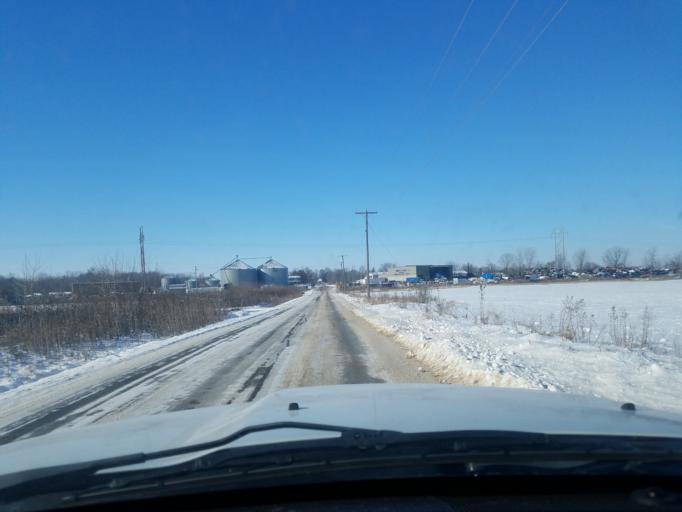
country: US
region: Indiana
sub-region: Noble County
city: Kendallville
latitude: 41.4113
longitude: -85.2542
